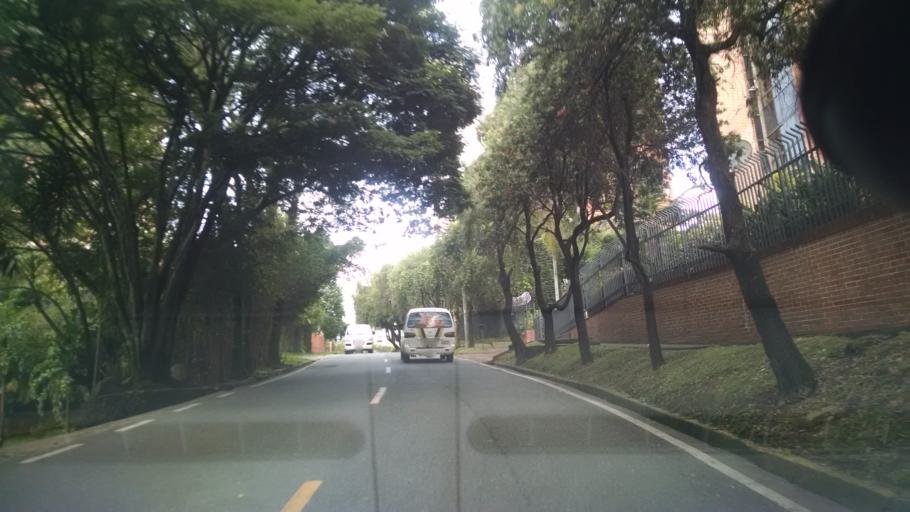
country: CO
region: Antioquia
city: Medellin
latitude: 6.2136
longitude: -75.5660
